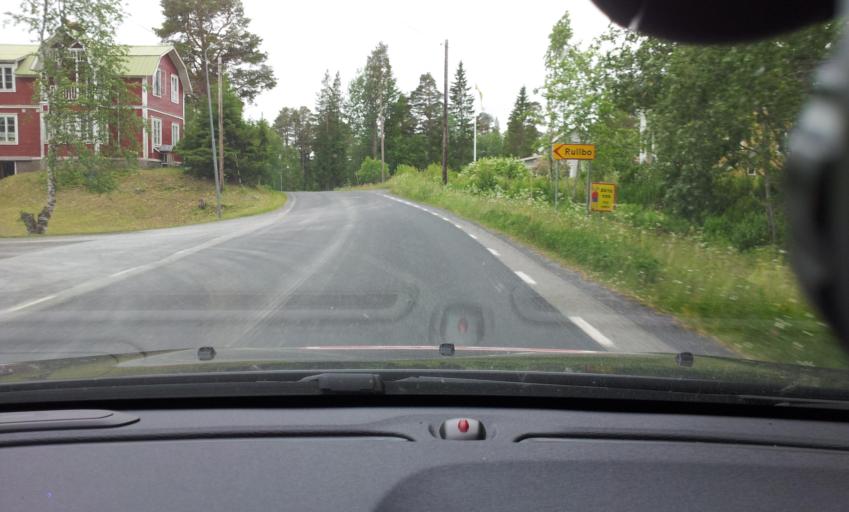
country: SE
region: Jaemtland
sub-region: Krokoms Kommun
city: Valla
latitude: 63.2830
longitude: 13.7689
